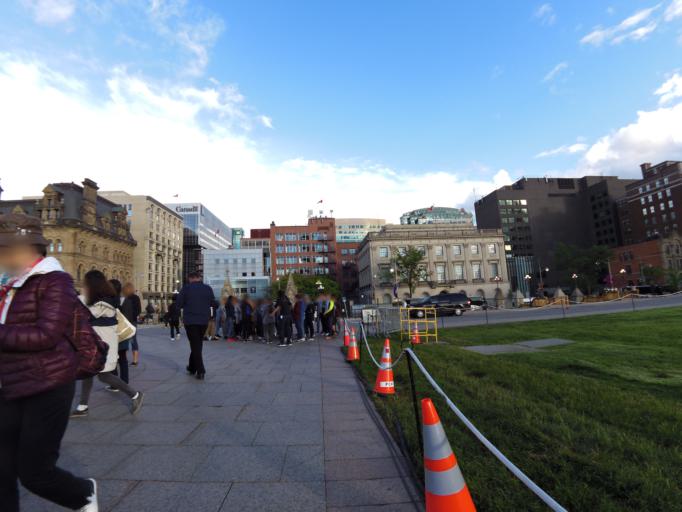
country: CA
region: Ontario
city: Ottawa
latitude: 45.4237
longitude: -75.6988
